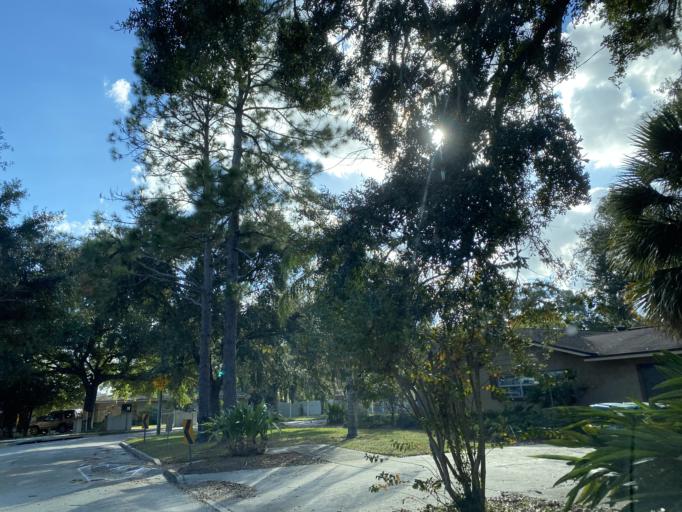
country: US
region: Florida
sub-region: Orange County
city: Orlando
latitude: 28.5497
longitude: -81.4026
